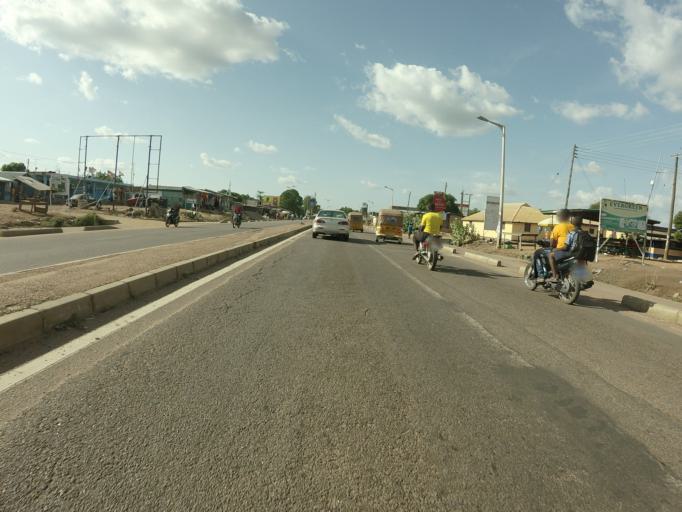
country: GH
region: Upper East
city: Bolgatanga
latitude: 10.7789
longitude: -0.8543
